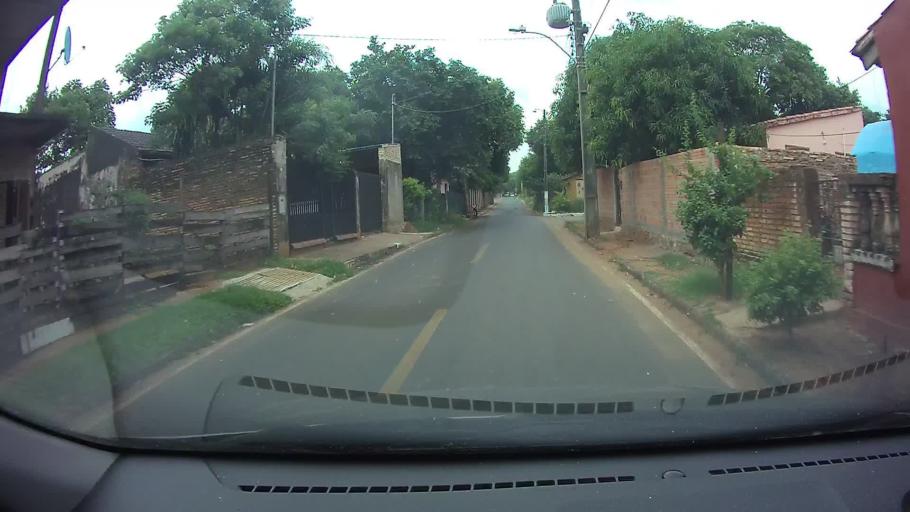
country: PY
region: Central
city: San Lorenzo
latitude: -25.2816
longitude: -57.4820
